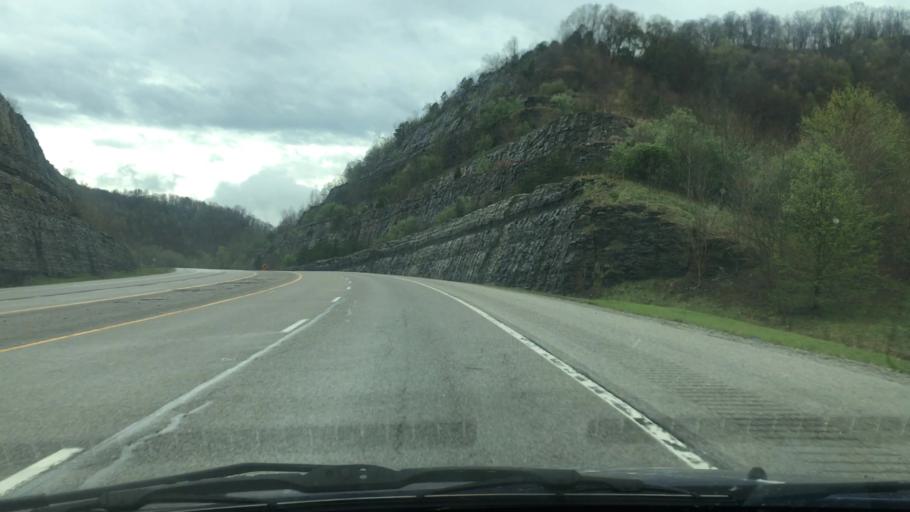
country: US
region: Kentucky
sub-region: Letcher County
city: Jenkins
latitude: 37.2168
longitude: -82.6275
